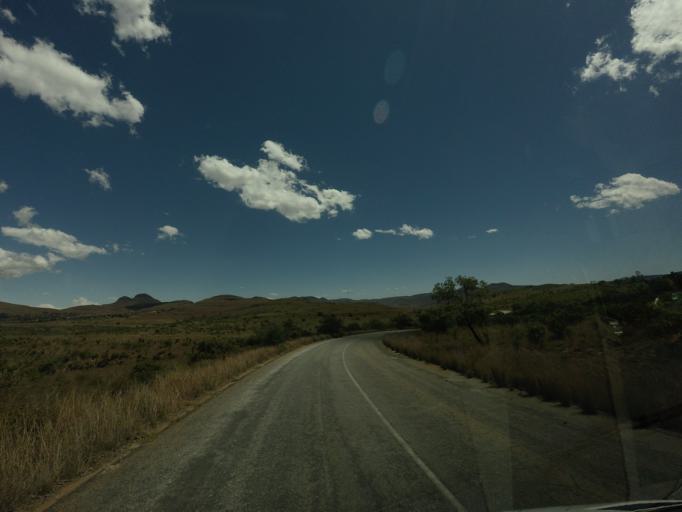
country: ZA
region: Limpopo
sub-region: Mopani District Municipality
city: Hoedspruit
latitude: -24.5909
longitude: 30.7913
